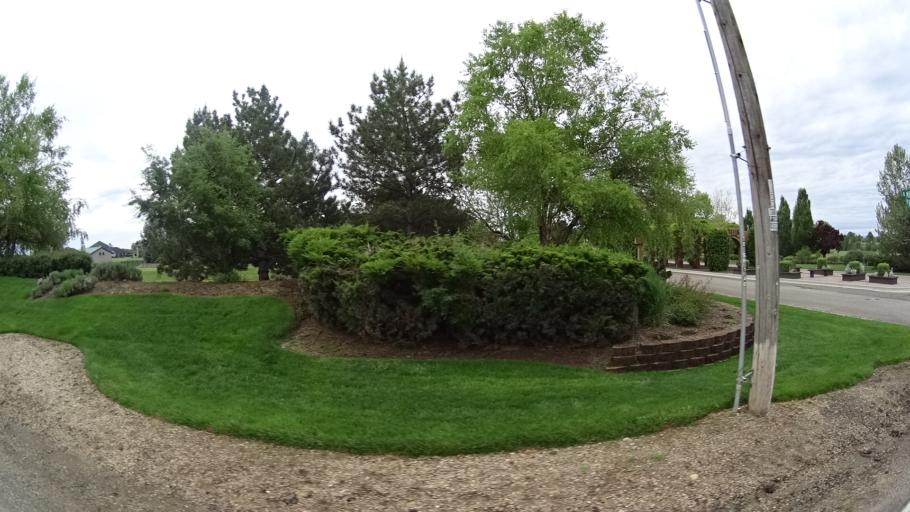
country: US
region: Idaho
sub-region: Ada County
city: Star
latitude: 43.7211
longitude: -116.4641
